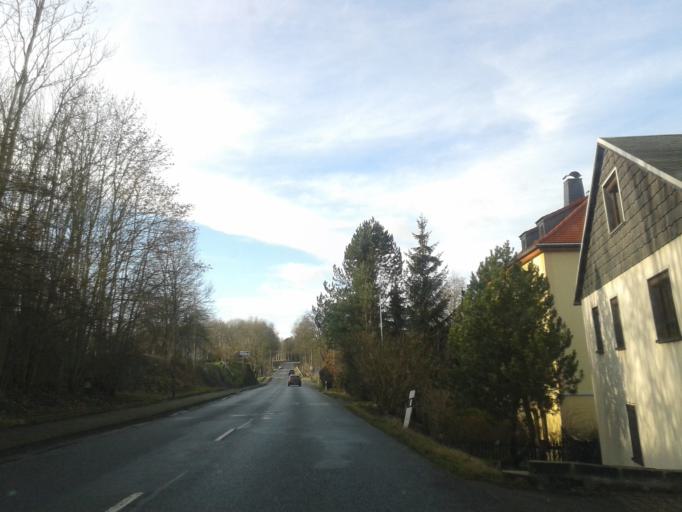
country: DE
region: Saxony
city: Eibau
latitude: 50.9743
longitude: 14.6806
